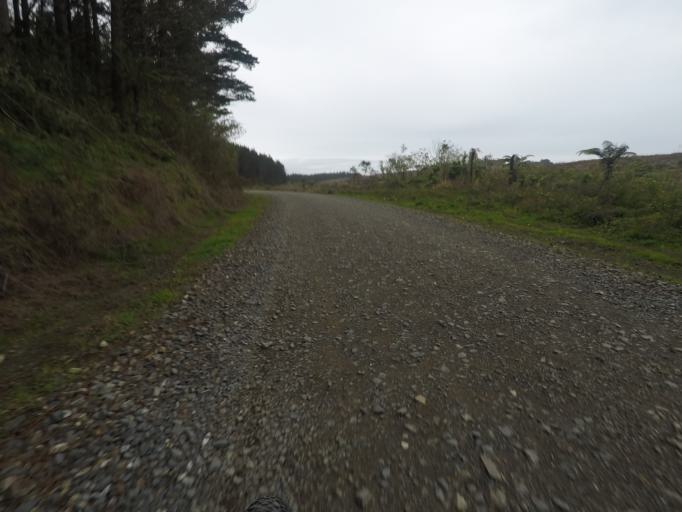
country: NZ
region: Auckland
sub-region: Auckland
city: Muriwai Beach
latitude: -36.7484
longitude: 174.5756
